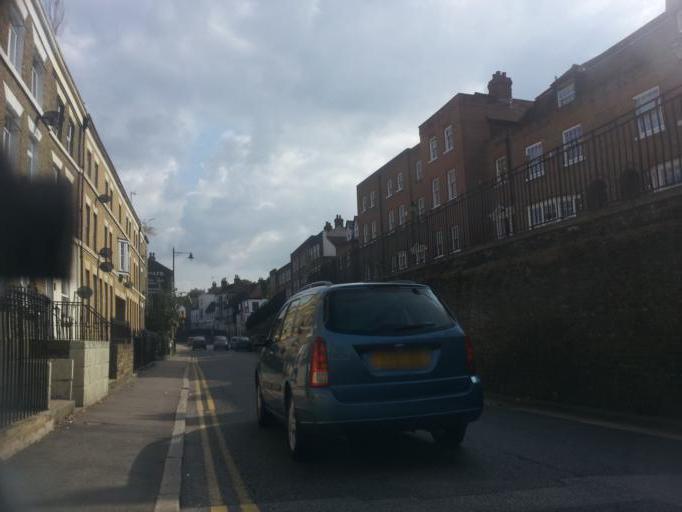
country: GB
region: England
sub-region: Medway
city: Rochester
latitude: 51.3848
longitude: 0.5101
